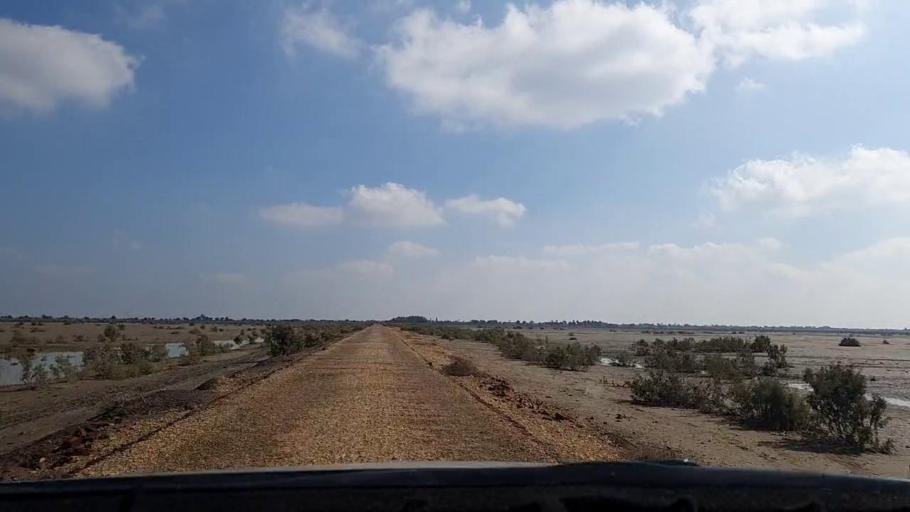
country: PK
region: Sindh
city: Pithoro
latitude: 25.7361
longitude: 69.2788
